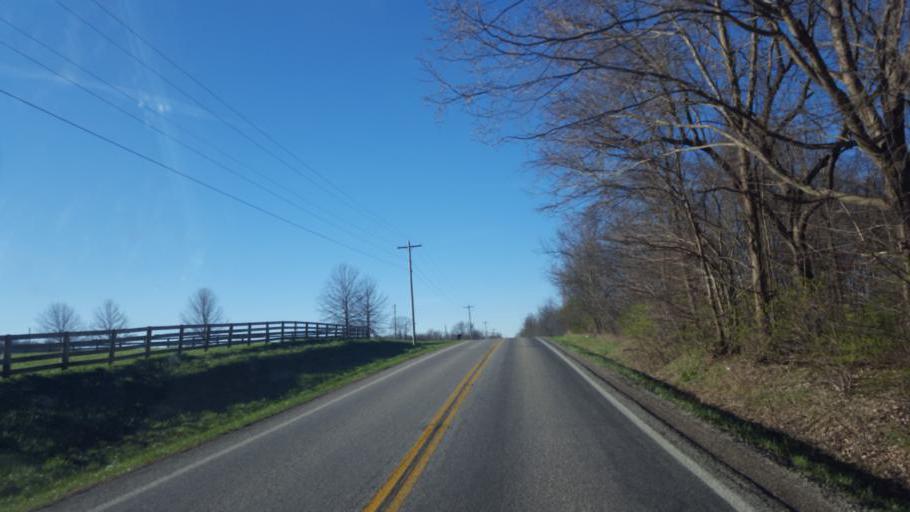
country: US
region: Ohio
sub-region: Morrow County
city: Mount Gilead
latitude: 40.4983
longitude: -82.8197
